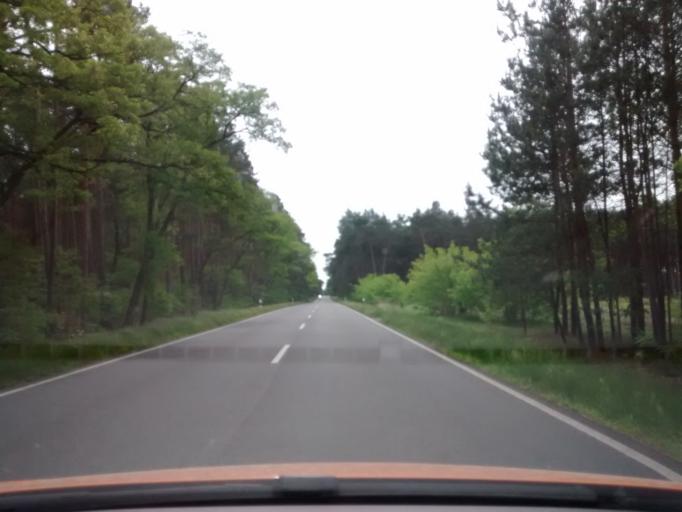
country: DE
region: Saxony-Anhalt
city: Holzdorf
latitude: 51.8717
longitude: 13.1446
